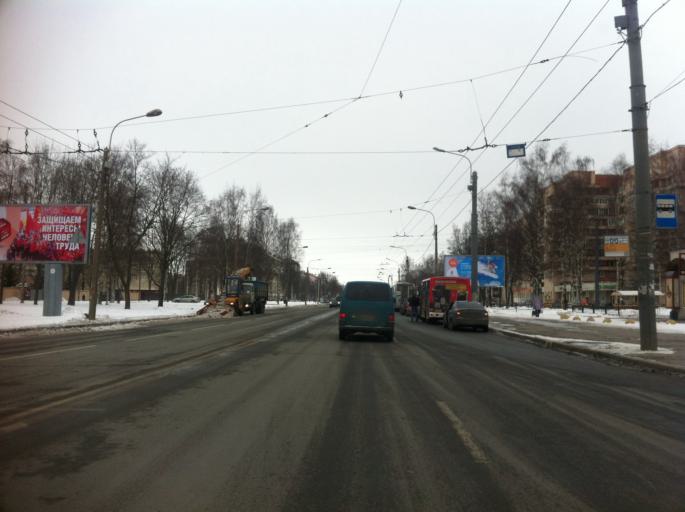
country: RU
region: St.-Petersburg
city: Uritsk
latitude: 59.8334
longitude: 30.1757
